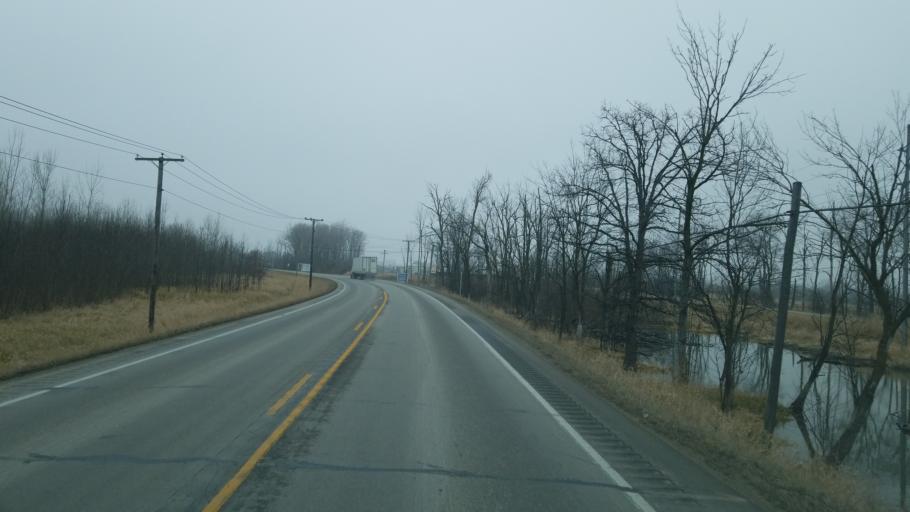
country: US
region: Indiana
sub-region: Adams County
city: Geneva
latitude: 40.5781
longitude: -84.9585
